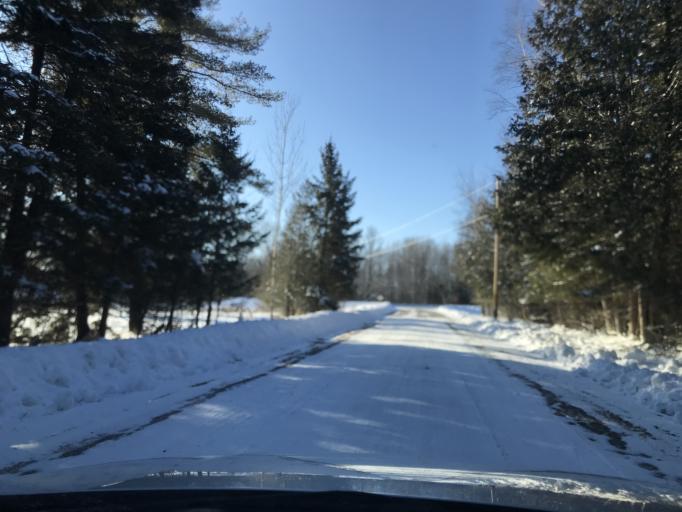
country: US
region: Wisconsin
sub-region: Oconto County
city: Oconto
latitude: 44.9514
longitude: -87.9771
